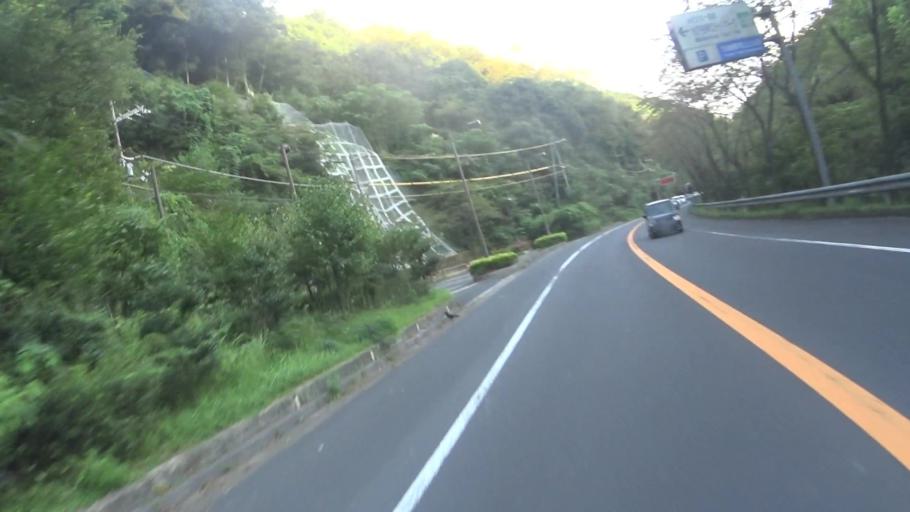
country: JP
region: Kyoto
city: Miyazu
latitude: 35.5457
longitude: 135.1109
